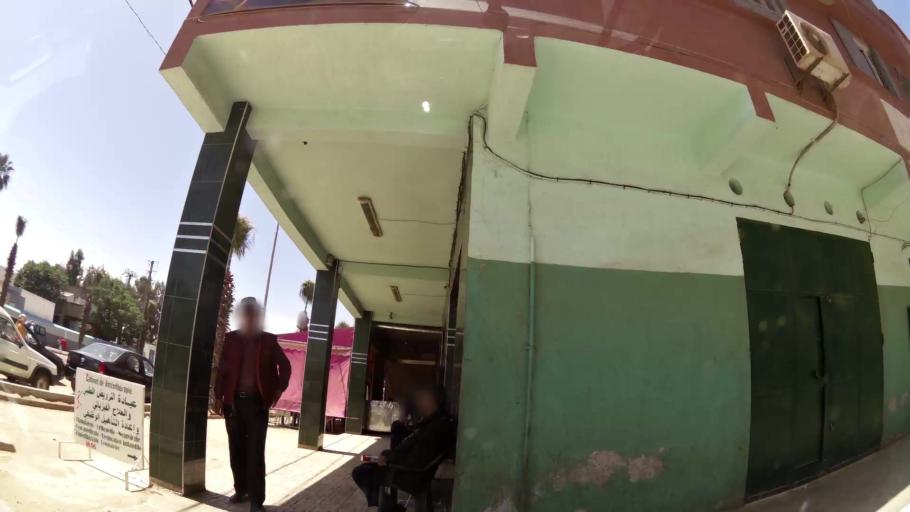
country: MA
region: Rabat-Sale-Zemmour-Zaer
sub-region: Khemisset
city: Khemisset
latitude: 33.8328
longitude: -6.0660
